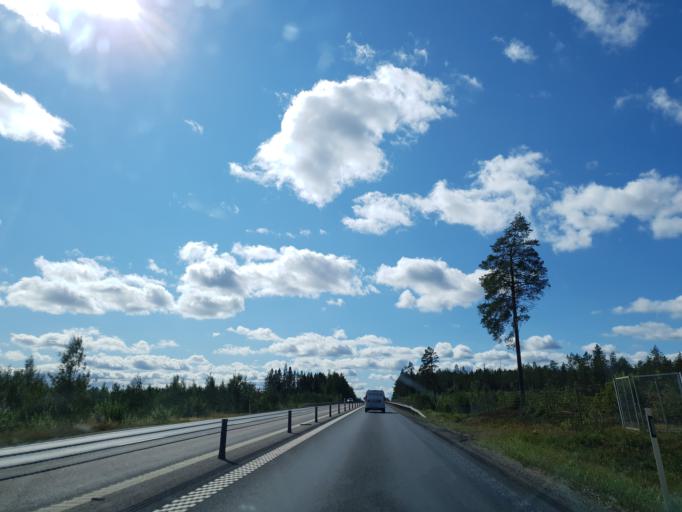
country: SE
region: Vaesterbotten
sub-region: Nordmalings Kommun
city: Nordmaling
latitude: 63.5098
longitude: 19.3543
